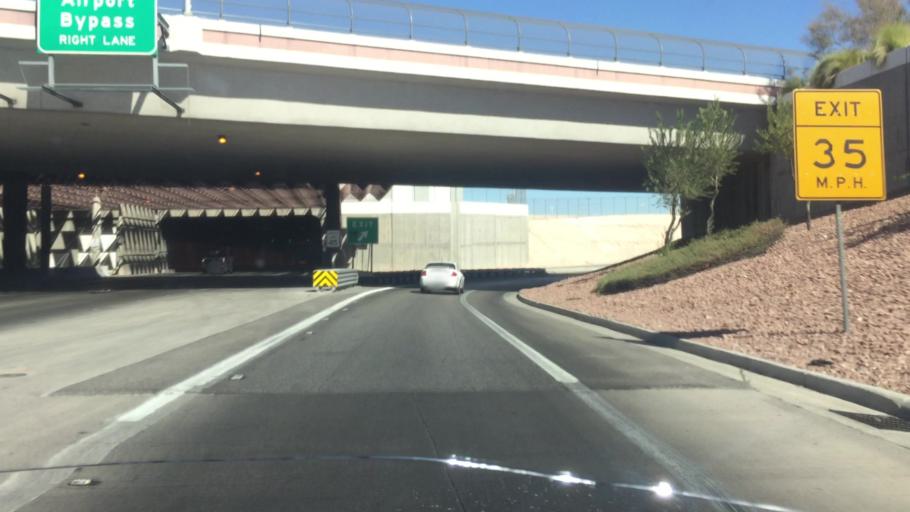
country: US
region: Nevada
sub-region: Clark County
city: Paradise
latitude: 36.0710
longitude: -115.1461
